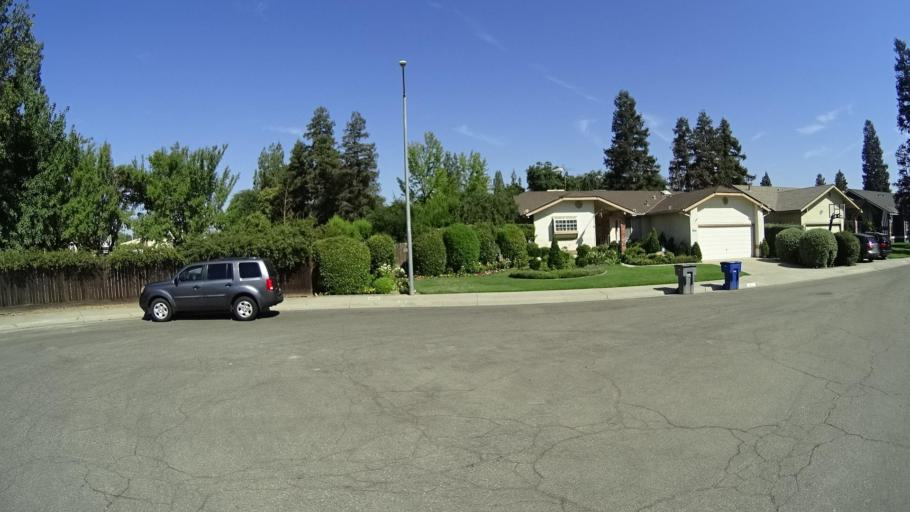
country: US
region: California
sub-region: Fresno County
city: Sunnyside
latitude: 36.7443
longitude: -119.6807
